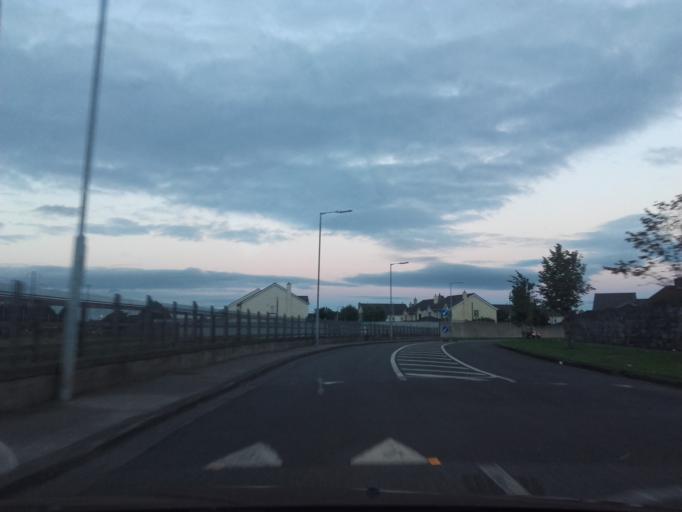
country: IE
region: Leinster
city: Tallaght
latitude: 53.2937
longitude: -6.3927
